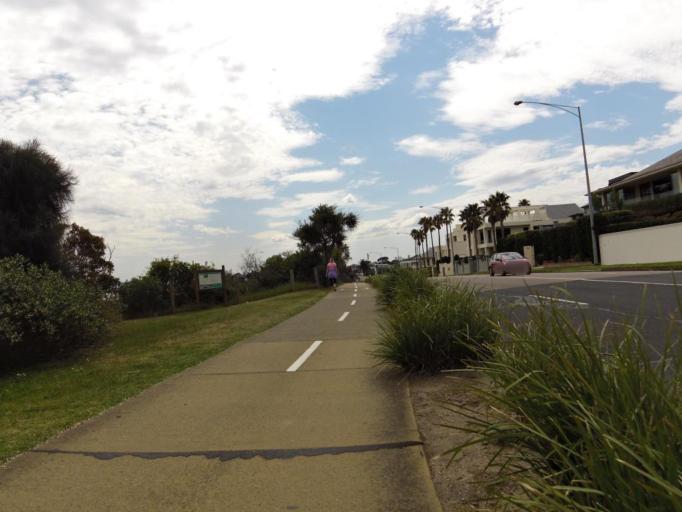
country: AU
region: Victoria
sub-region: Bayside
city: Hampton
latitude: -37.9222
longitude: 144.9877
